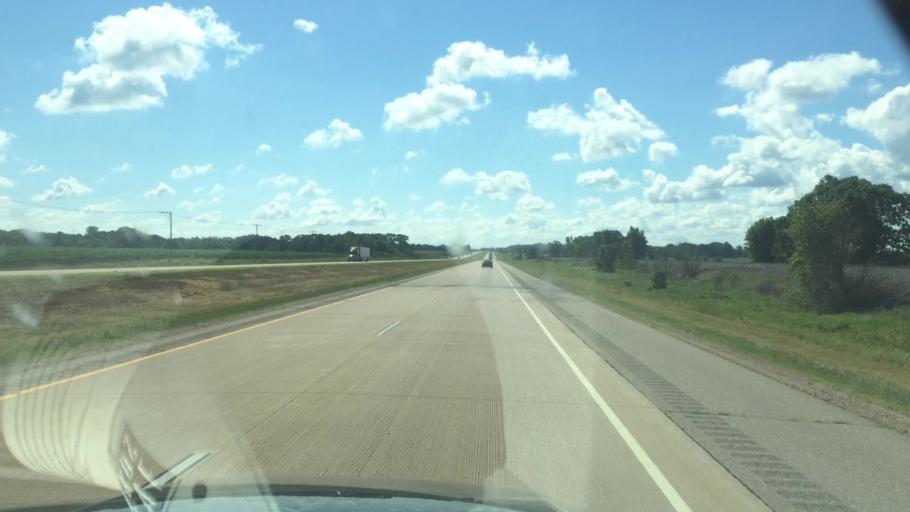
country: US
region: Wisconsin
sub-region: Portage County
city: Amherst
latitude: 44.4917
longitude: -89.3616
